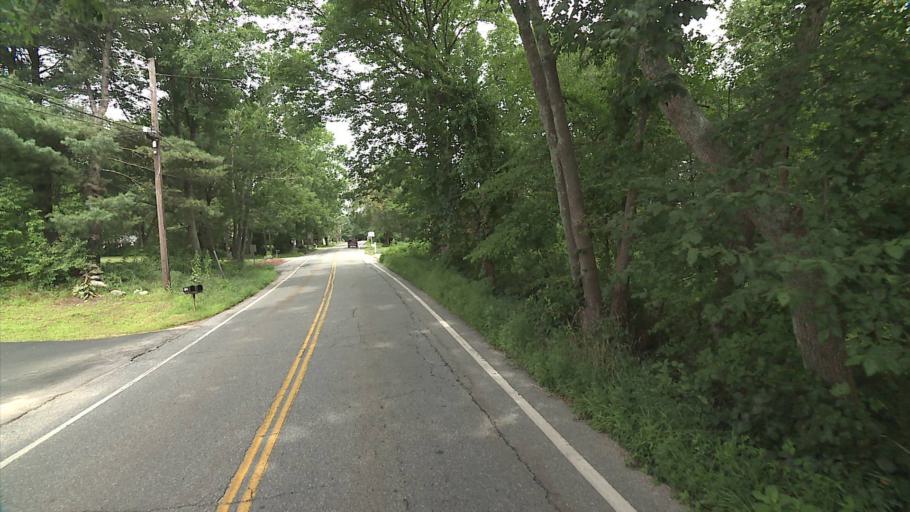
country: US
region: Massachusetts
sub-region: Worcester County
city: Webster
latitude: 42.0232
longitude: -71.8450
